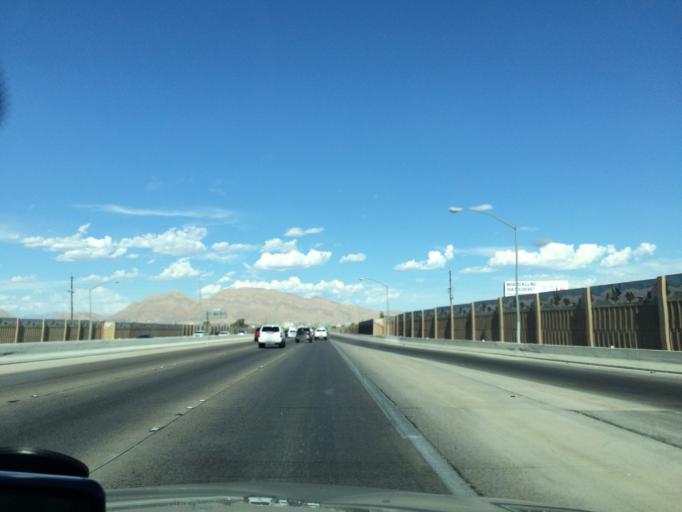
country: US
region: Nevada
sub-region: Clark County
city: Las Vegas
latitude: 36.1678
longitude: -115.1134
